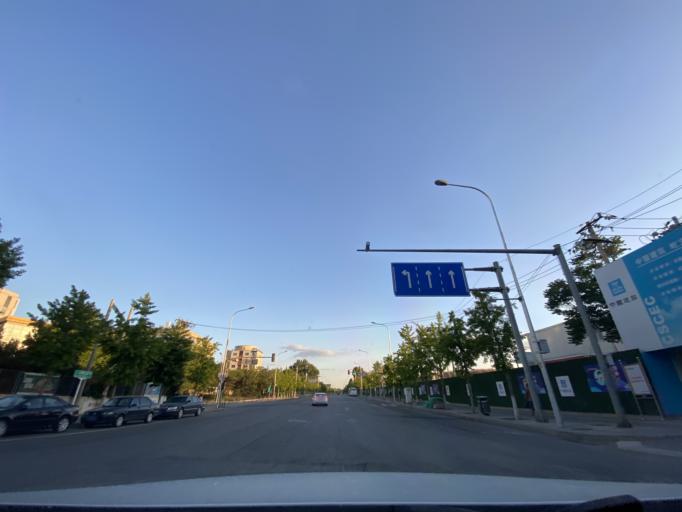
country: CN
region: Beijing
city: Sijiqing
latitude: 39.9532
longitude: 116.2631
